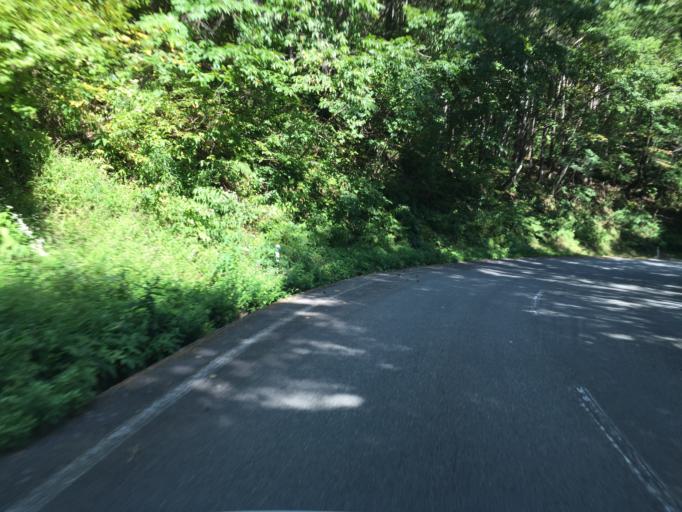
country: JP
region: Fukushima
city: Inawashiro
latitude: 37.6594
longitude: 140.1501
